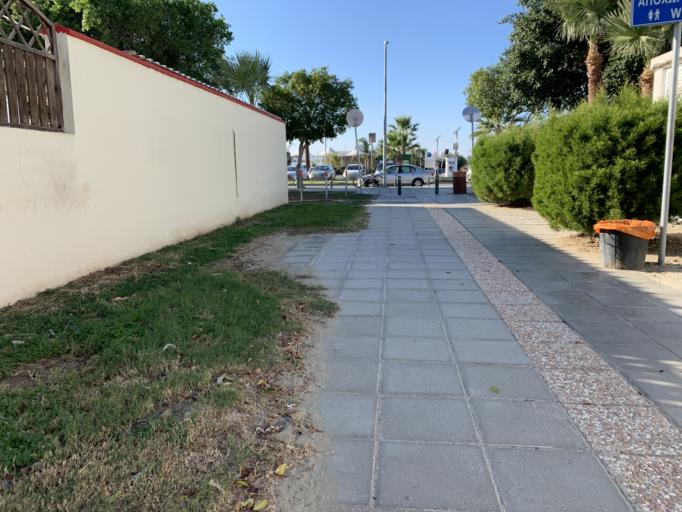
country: CY
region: Larnaka
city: Larnaca
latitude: 34.8891
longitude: 33.6368
